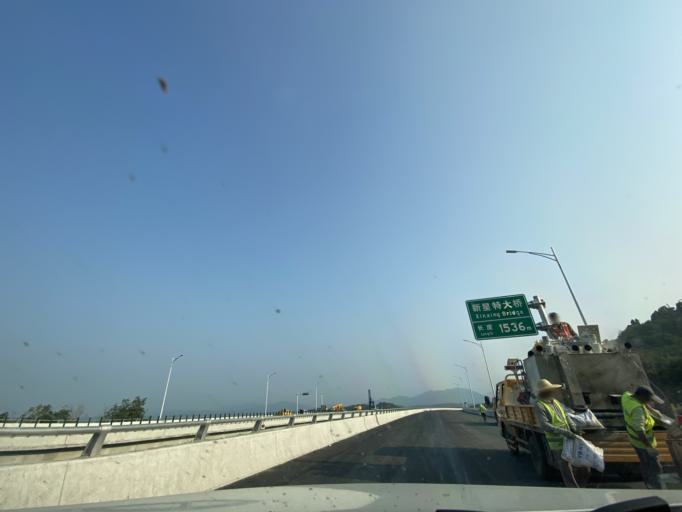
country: CN
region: Hainan
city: Xiangshui
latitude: 18.6624
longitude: 109.6284
